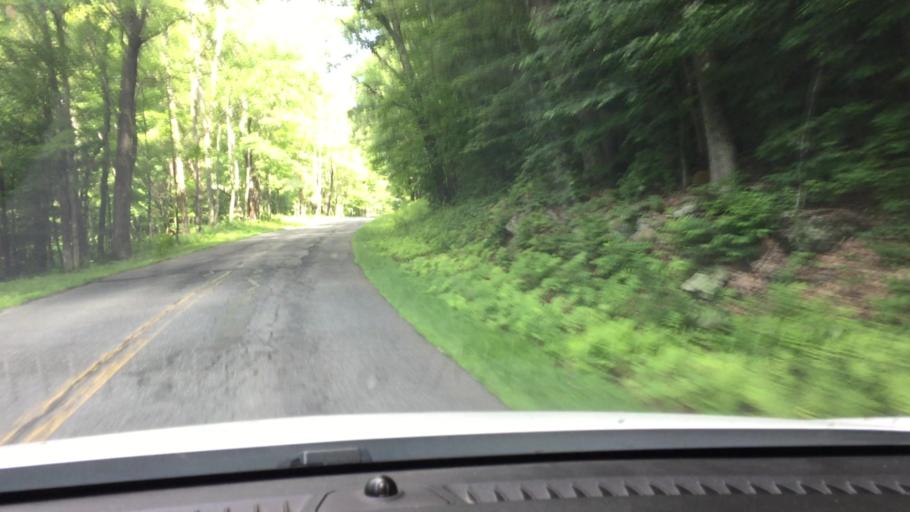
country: US
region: Massachusetts
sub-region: Berkshire County
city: Otis
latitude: 42.2045
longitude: -73.1667
